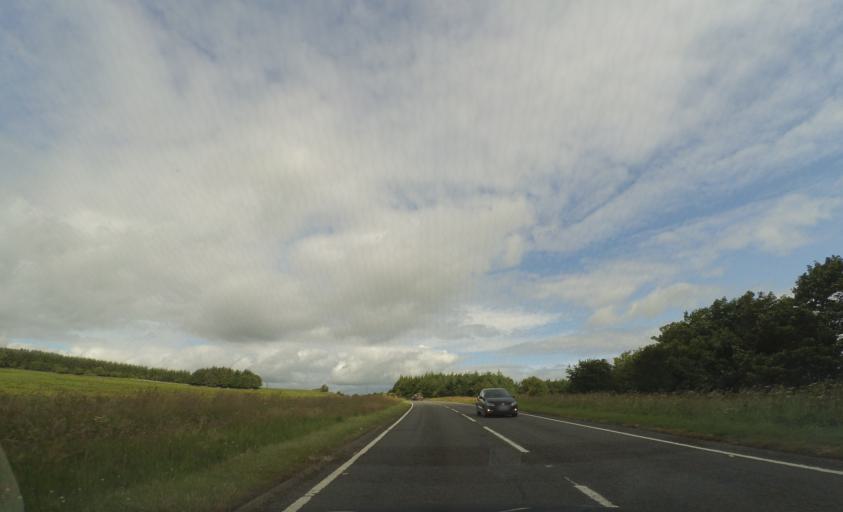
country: GB
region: Scotland
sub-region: The Scottish Borders
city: Hawick
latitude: 55.4695
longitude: -2.7922
